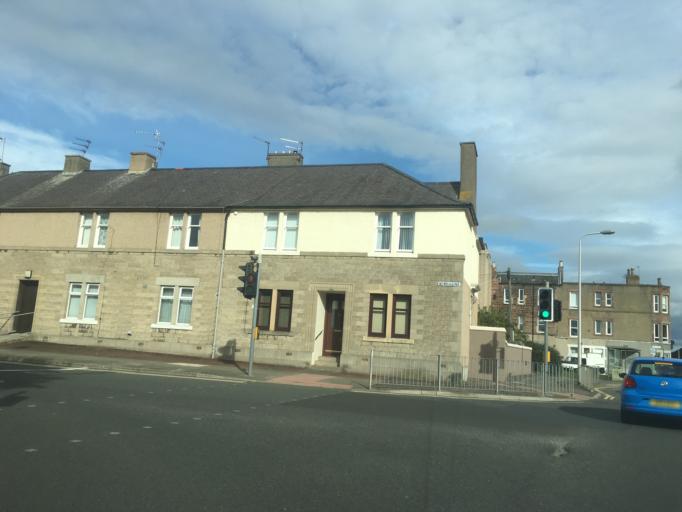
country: GB
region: Scotland
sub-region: East Lothian
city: Musselburgh
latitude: 55.9404
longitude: -3.0473
